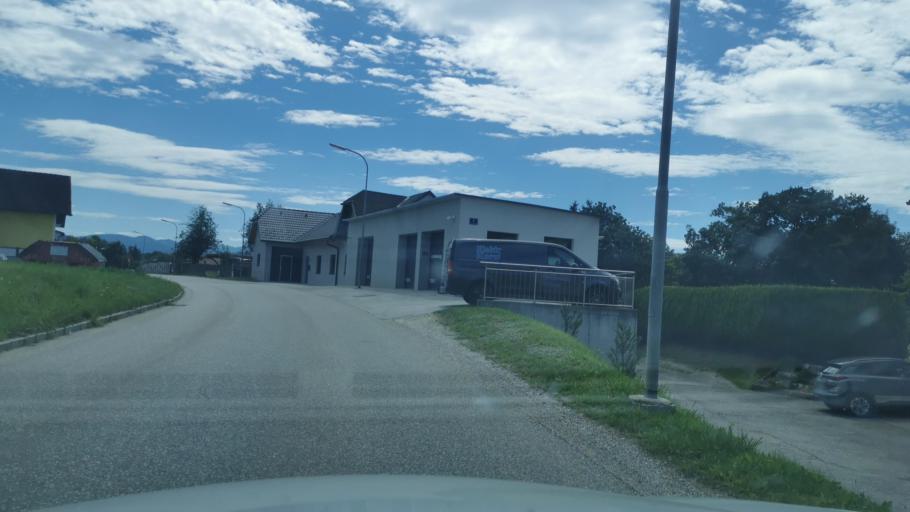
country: AT
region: Lower Austria
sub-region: Politischer Bezirk Sankt Polten
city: Pyhra
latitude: 48.1501
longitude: 15.6411
